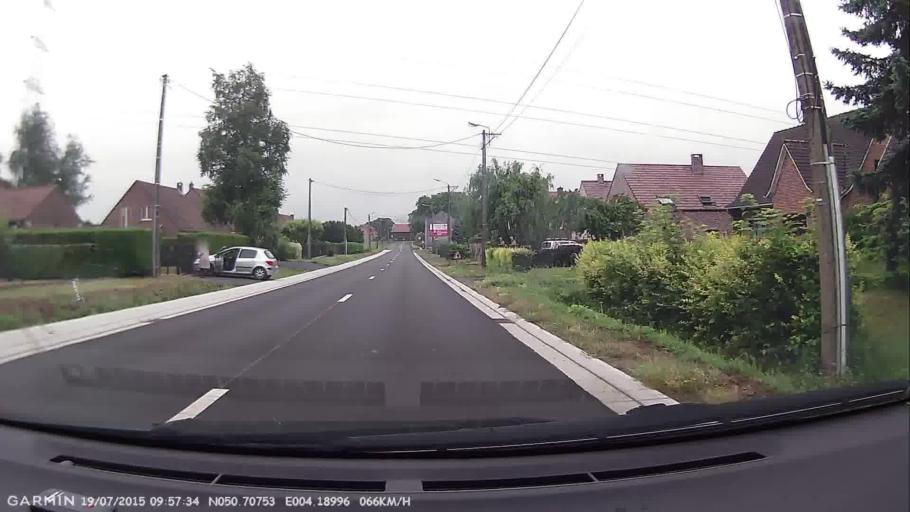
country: BE
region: Wallonia
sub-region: Province du Brabant Wallon
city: Tubize
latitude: 50.7075
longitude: 4.1901
